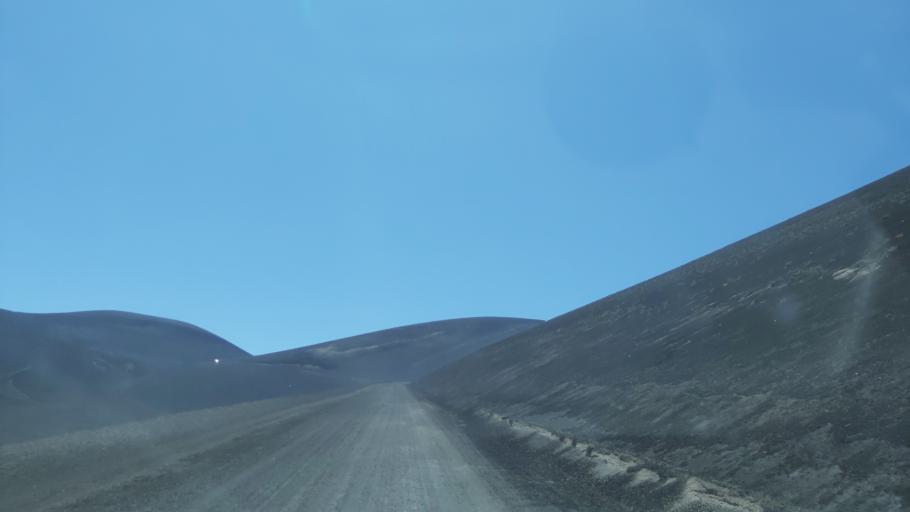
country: CL
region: Araucania
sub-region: Provincia de Cautin
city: Vilcun
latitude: -38.3961
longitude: -71.5456
